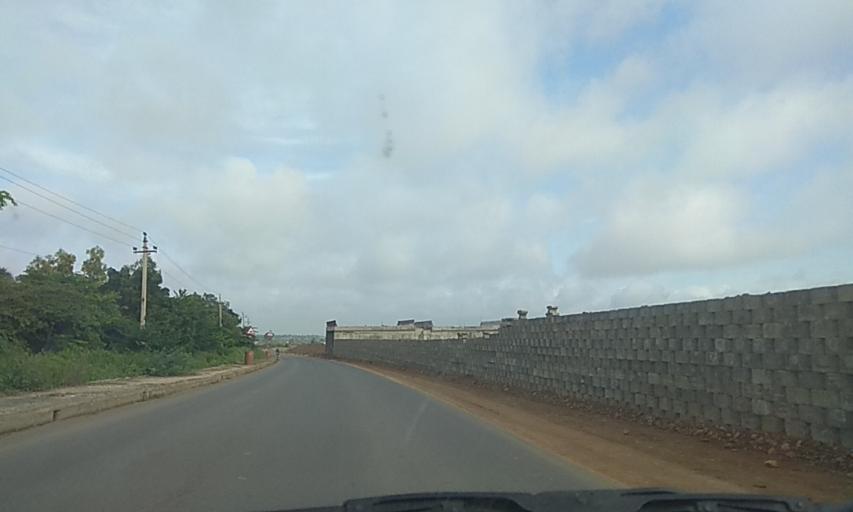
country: IN
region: Karnataka
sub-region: Haveri
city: Haveri
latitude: 14.8535
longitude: 75.3287
